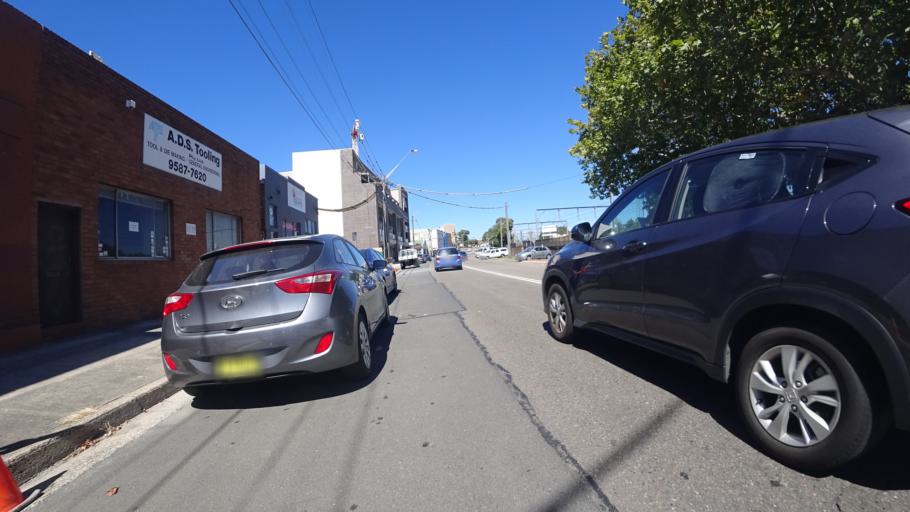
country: AU
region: New South Wales
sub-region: Kogarah
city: Beverly Park
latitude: -33.9672
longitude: 151.1296
